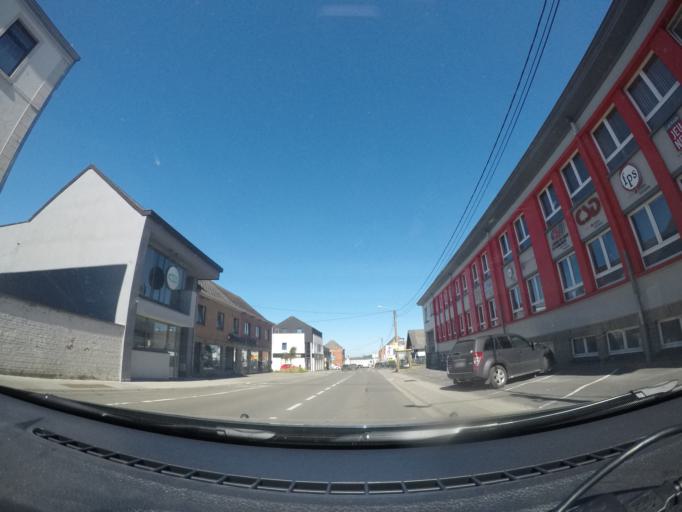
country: BE
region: Wallonia
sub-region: Province de Namur
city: Philippeville
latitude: 50.1961
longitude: 4.5394
